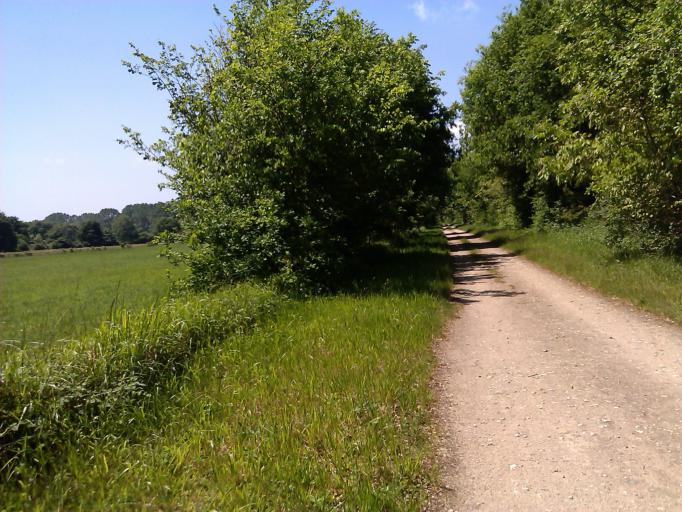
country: FR
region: Centre
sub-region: Departement de l'Indre
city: Saint-Gaultier
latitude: 46.6401
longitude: 1.3864
